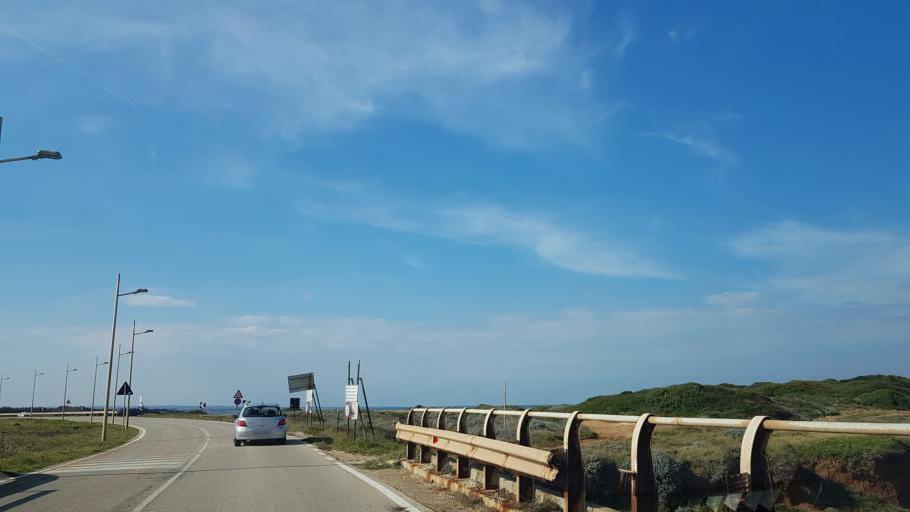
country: IT
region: Apulia
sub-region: Provincia di Brindisi
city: Brindisi
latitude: 40.6863
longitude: 17.8699
